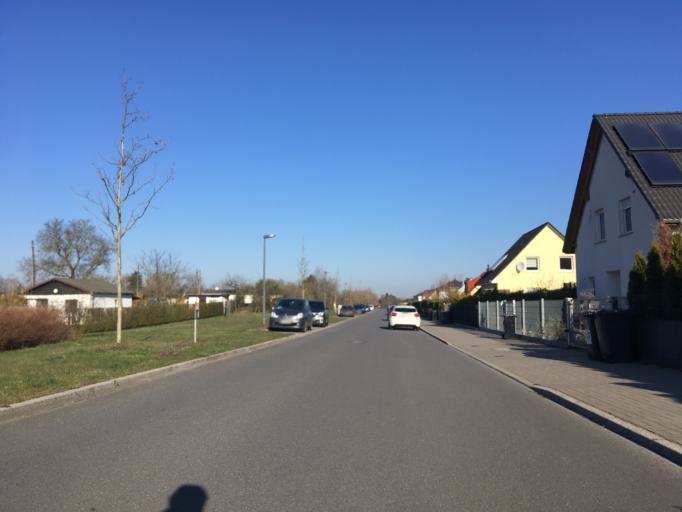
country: DE
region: Berlin
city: Buchholz
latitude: 52.6167
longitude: 13.4236
